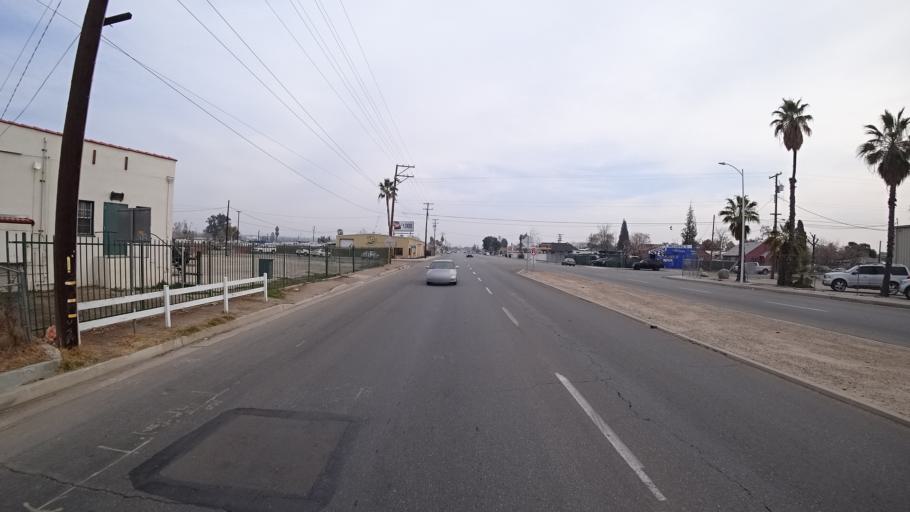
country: US
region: California
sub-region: Kern County
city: Bakersfield
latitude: 35.3733
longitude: -118.9897
